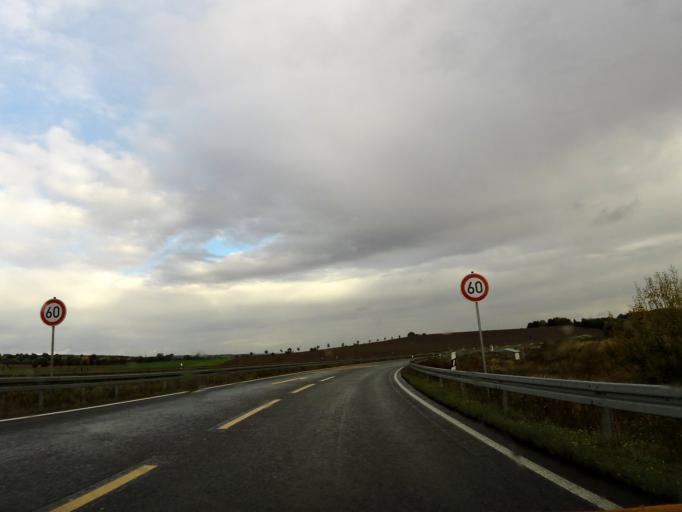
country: DE
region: Lower Saxony
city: Rosdorf
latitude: 51.4555
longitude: 9.8628
